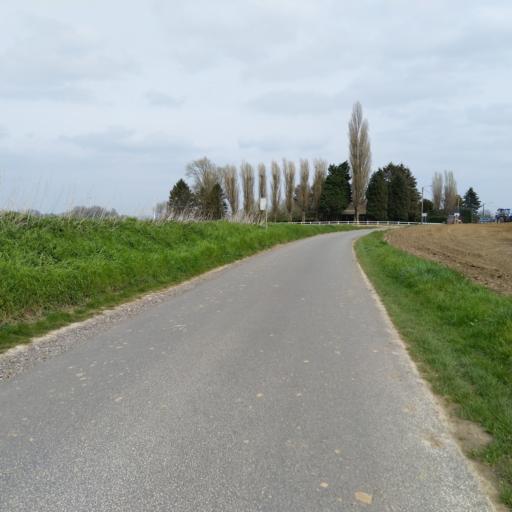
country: BE
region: Wallonia
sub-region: Province du Hainaut
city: Quevy-le-Petit
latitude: 50.3563
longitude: 3.9385
